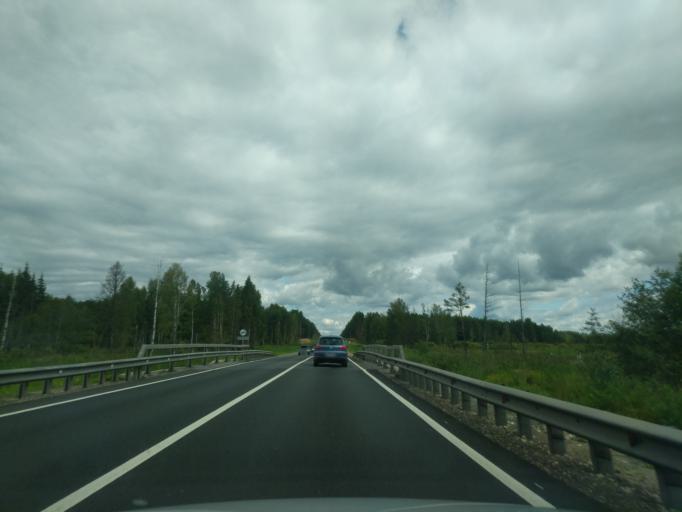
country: RU
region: Jaroslavl
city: Nekrasovskoye
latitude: 57.5745
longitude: 40.2738
